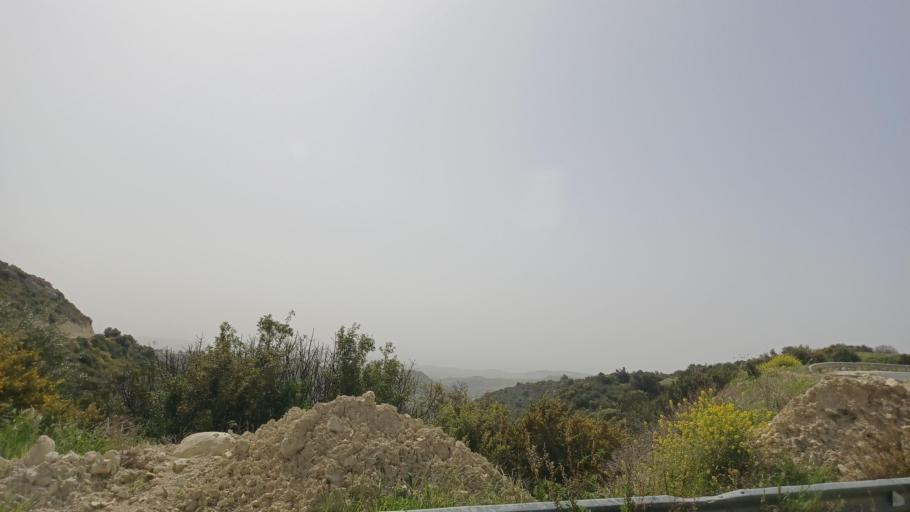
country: CY
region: Limassol
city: Pissouri
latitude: 34.7181
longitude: 32.7175
